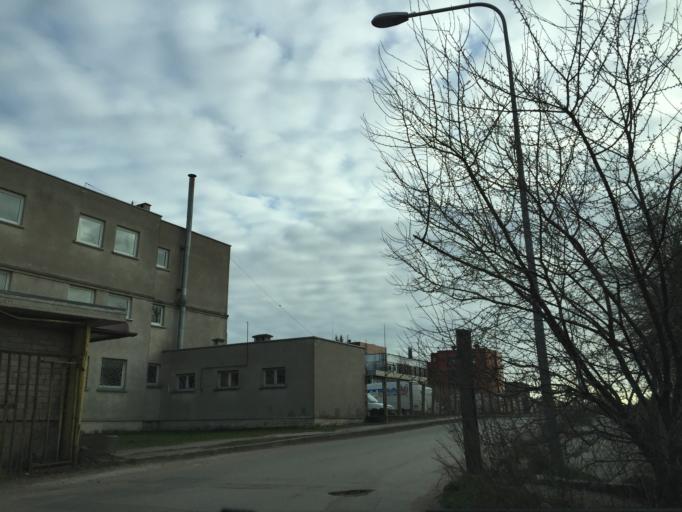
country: LT
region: Klaipedos apskritis
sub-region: Klaipeda
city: Klaipeda
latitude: 55.6971
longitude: 21.1767
